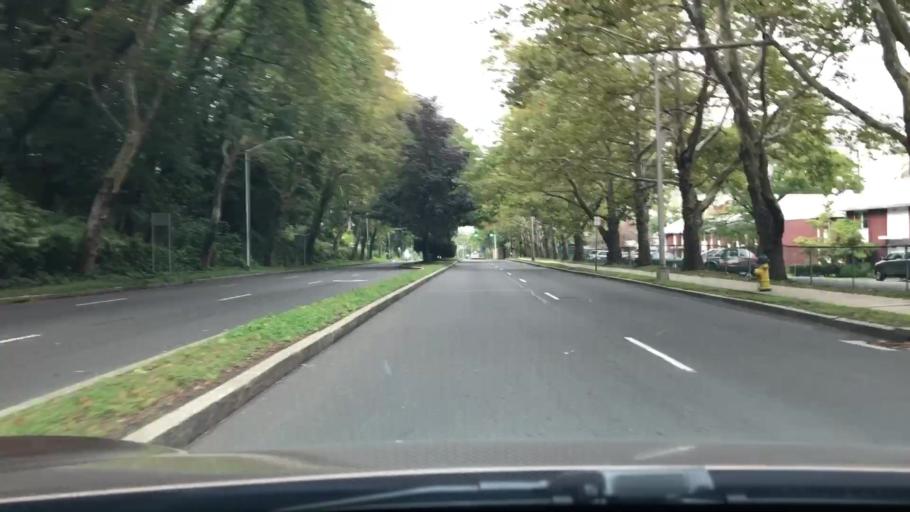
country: US
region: Connecticut
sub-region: Fairfield County
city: Norwalk
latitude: 41.0969
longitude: -73.4232
